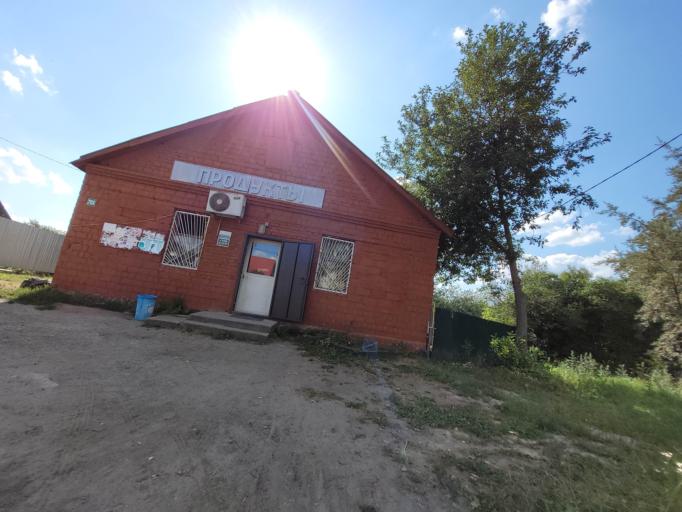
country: RU
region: Moskovskaya
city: Peski
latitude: 55.2280
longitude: 38.7500
